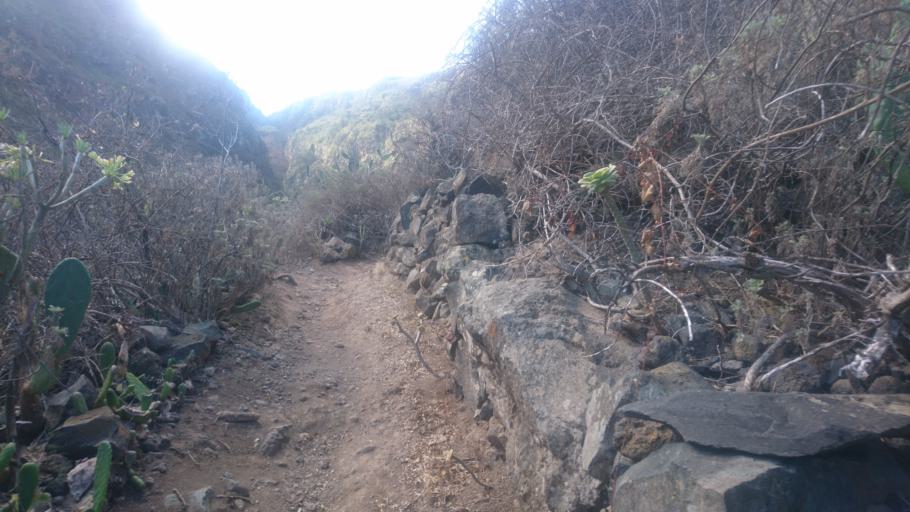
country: ES
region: Canary Islands
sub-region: Provincia de Santa Cruz de Tenerife
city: San Juan de la Rambla
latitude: 28.3896
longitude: -16.6267
